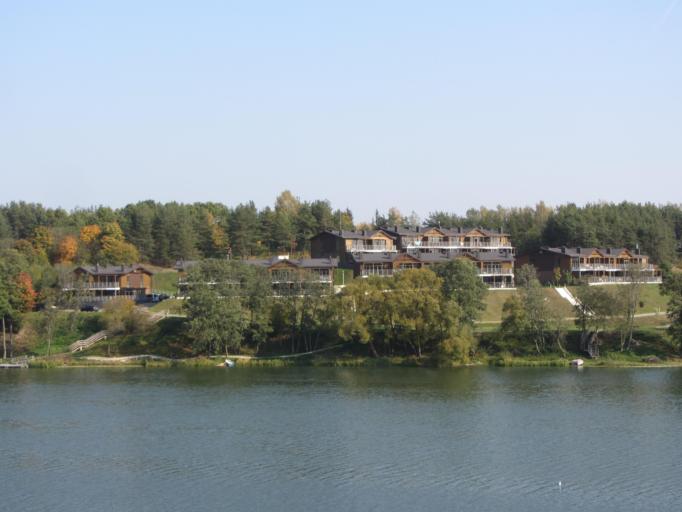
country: LT
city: Trakai
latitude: 54.6256
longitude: 24.9236
